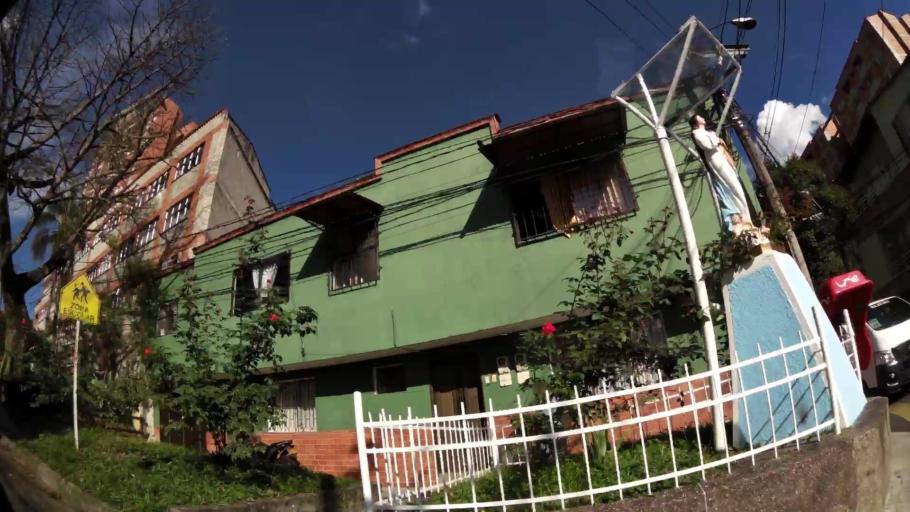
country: CO
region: Antioquia
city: Envigado
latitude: 6.1676
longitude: -75.5787
